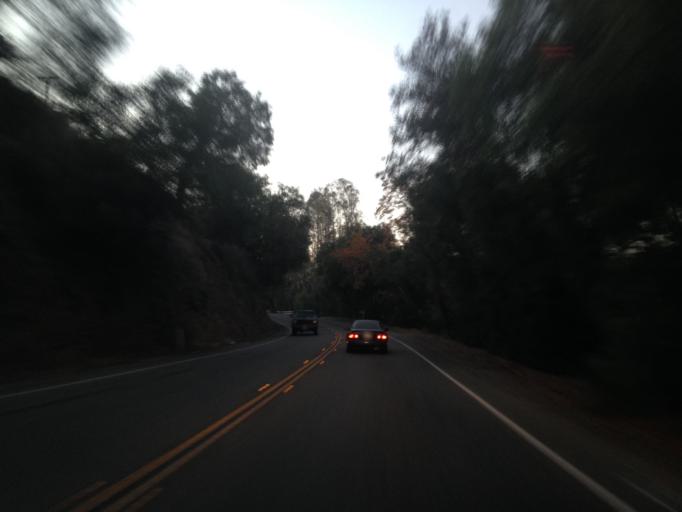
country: US
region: California
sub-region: San Diego County
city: Bonsall
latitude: 33.2554
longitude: -117.2085
